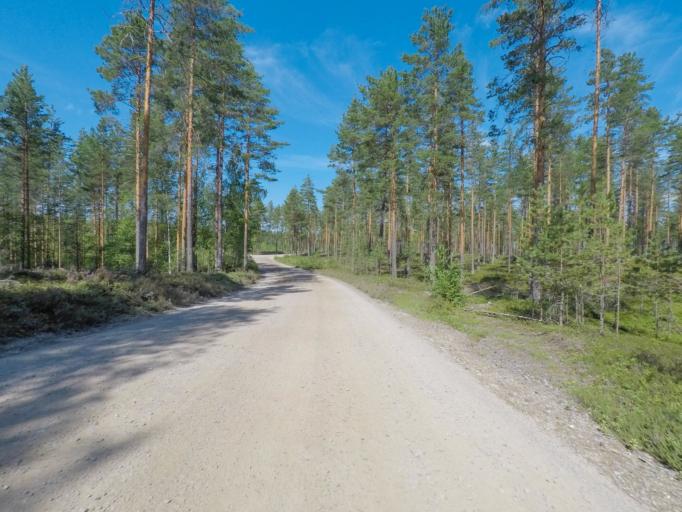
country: FI
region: Southern Savonia
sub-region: Mikkeli
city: Puumala
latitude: 61.4170
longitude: 28.0427
